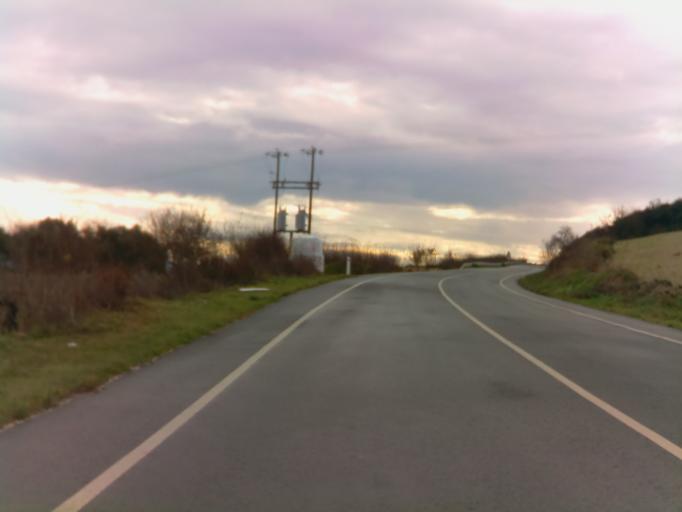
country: CY
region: Pafos
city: Pegeia
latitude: 34.9072
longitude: 32.4393
